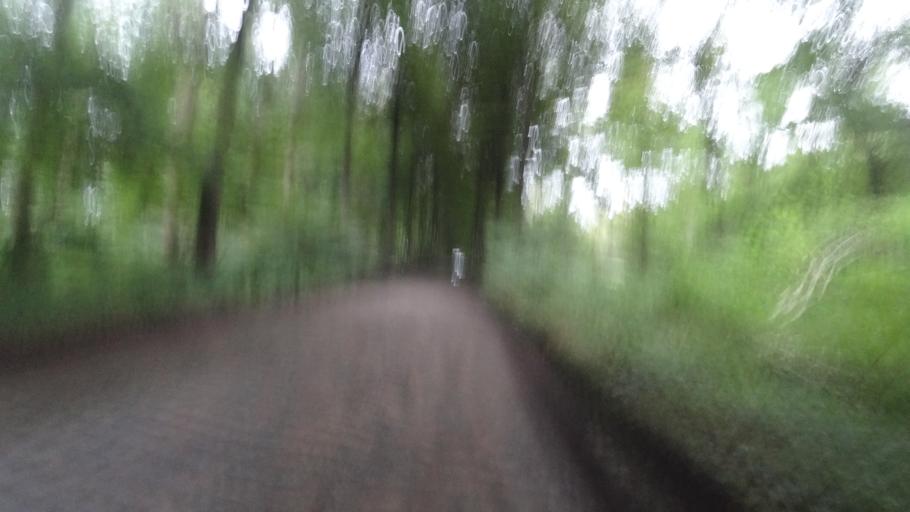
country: BE
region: Wallonia
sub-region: Province du Brabant Wallon
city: Walhain-Saint-Paul
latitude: 50.6092
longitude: 4.7391
